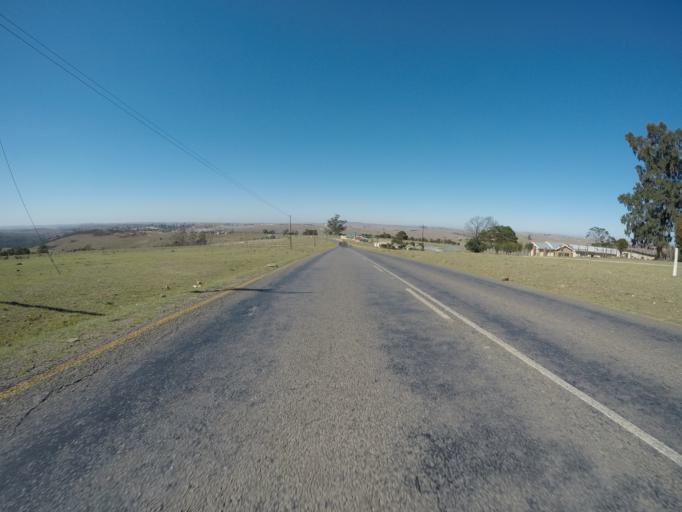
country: ZA
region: Eastern Cape
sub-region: OR Tambo District Municipality
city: Mthatha
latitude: -31.7935
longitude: 28.7451
